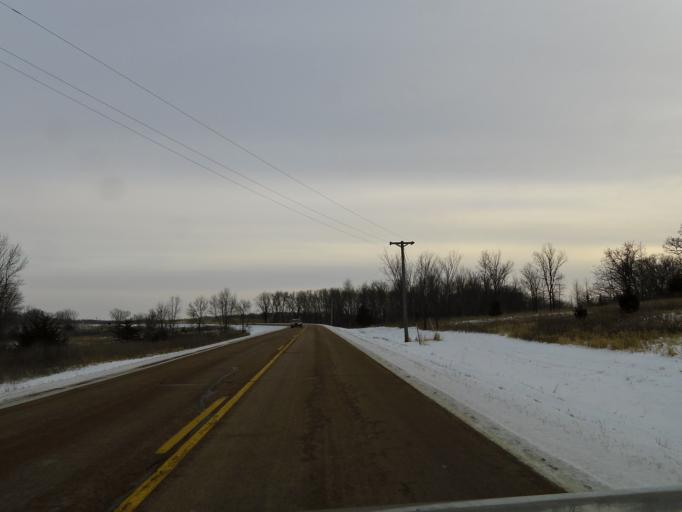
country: US
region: Minnesota
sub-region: Carver County
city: Victoria
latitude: 44.8827
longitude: -93.7031
